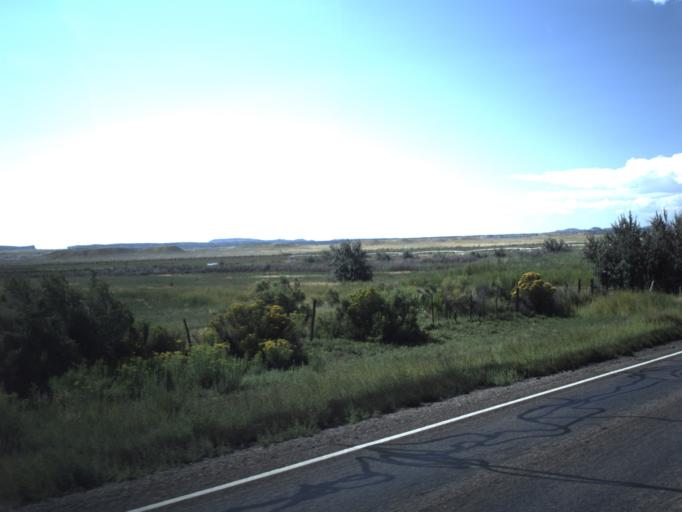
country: US
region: Utah
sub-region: Emery County
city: Ferron
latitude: 38.8685
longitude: -111.2962
